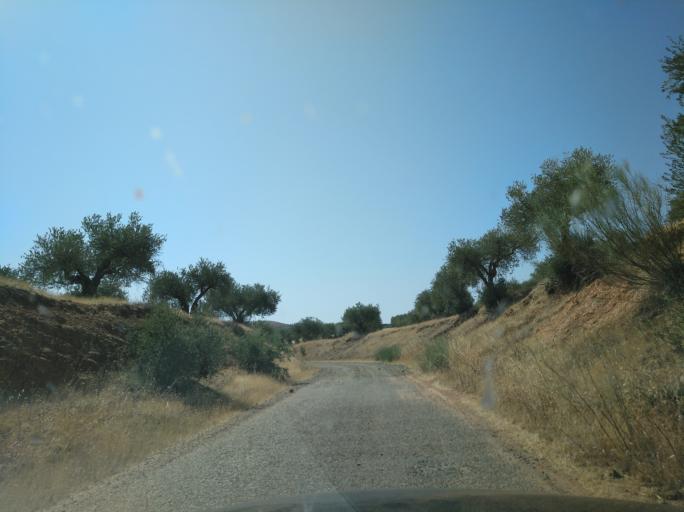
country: PT
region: Portalegre
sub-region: Campo Maior
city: Campo Maior
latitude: 39.0671
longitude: -7.0144
